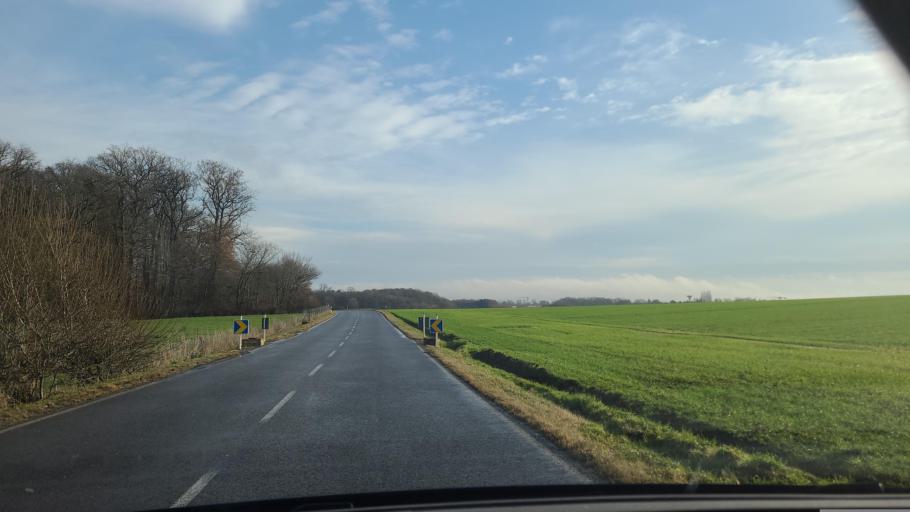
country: LU
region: Luxembourg
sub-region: Canton de Capellen
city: Koerich
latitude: 49.6522
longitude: 5.9653
